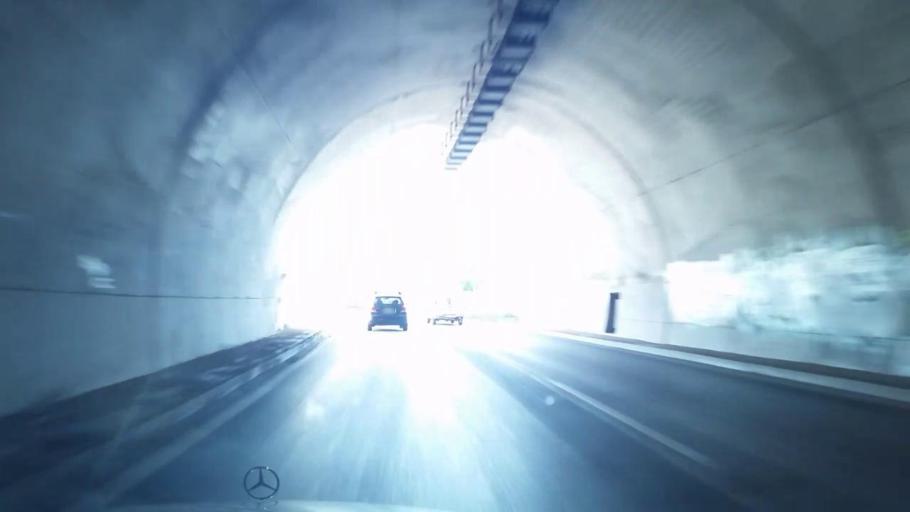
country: GR
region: Attica
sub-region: Nomarchia Anatolikis Attikis
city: Kitsi
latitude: 37.8602
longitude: 23.8430
